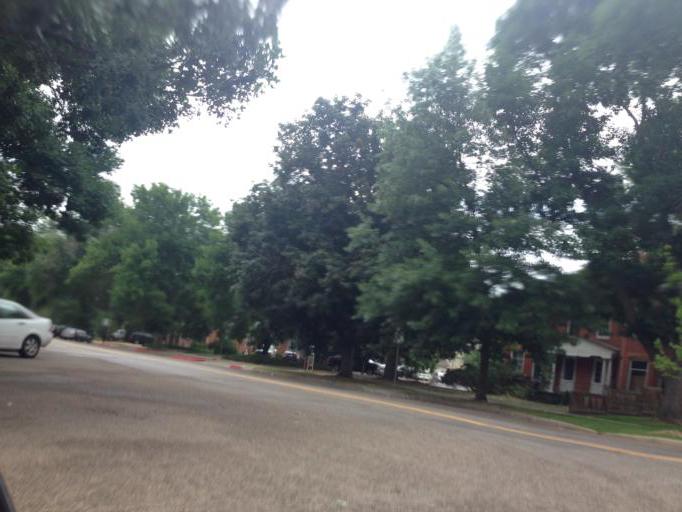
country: US
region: Colorado
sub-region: Larimer County
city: Fort Collins
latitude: 40.5789
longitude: -105.0827
